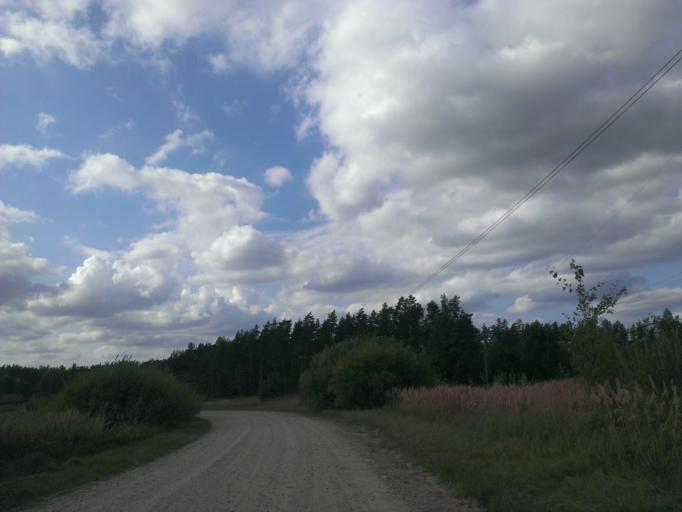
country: LV
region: Incukalns
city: Vangazi
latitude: 57.1202
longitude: 24.5680
